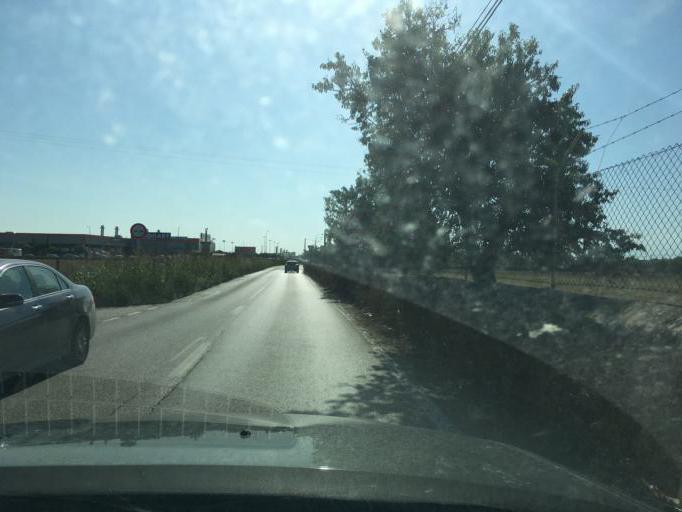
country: ES
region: Balearic Islands
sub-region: Illes Balears
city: Palma
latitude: 39.5760
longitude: 2.6851
